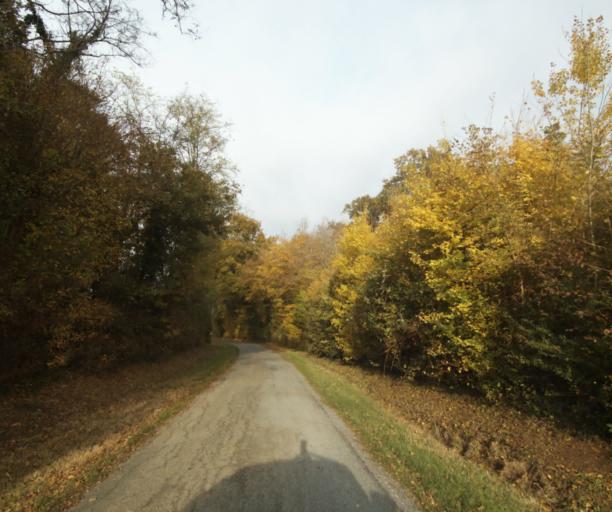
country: FR
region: Poitou-Charentes
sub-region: Departement de la Charente-Maritime
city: Nieul-les-Saintes
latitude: 45.7803
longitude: -0.7426
